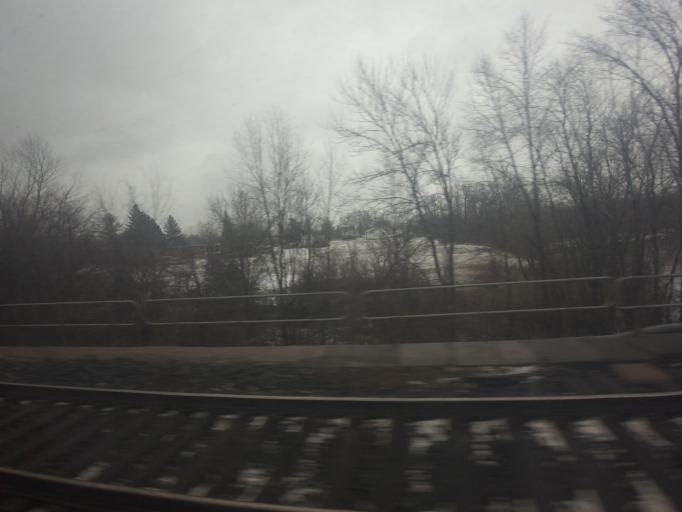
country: CA
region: Ontario
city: Deseronto
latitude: 44.2091
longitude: -77.2087
